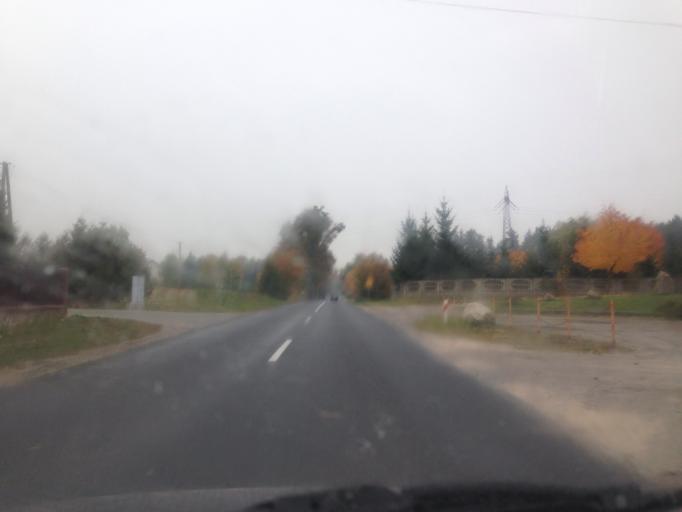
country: PL
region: Kujawsko-Pomorskie
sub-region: Powiat brodnicki
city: Bartniczka
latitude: 53.2515
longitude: 19.5964
